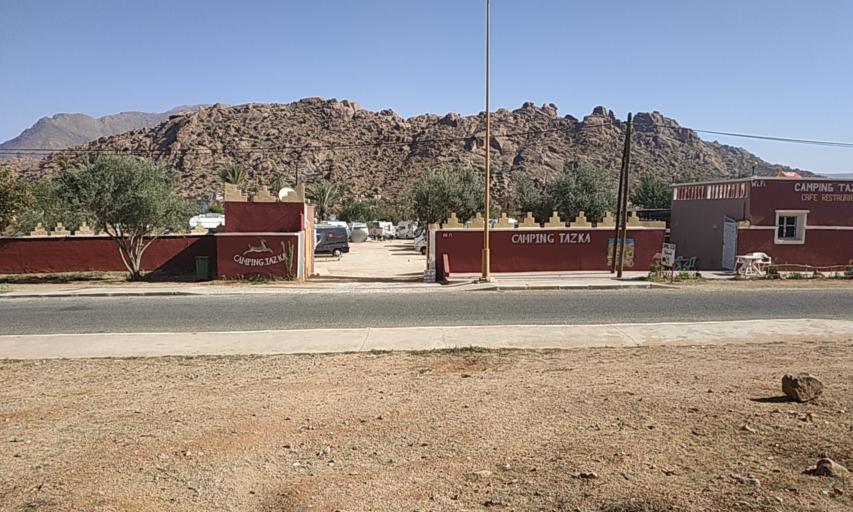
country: MA
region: Souss-Massa-Draa
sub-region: Tiznit
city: Tafraout
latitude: 29.7158
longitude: -8.9868
